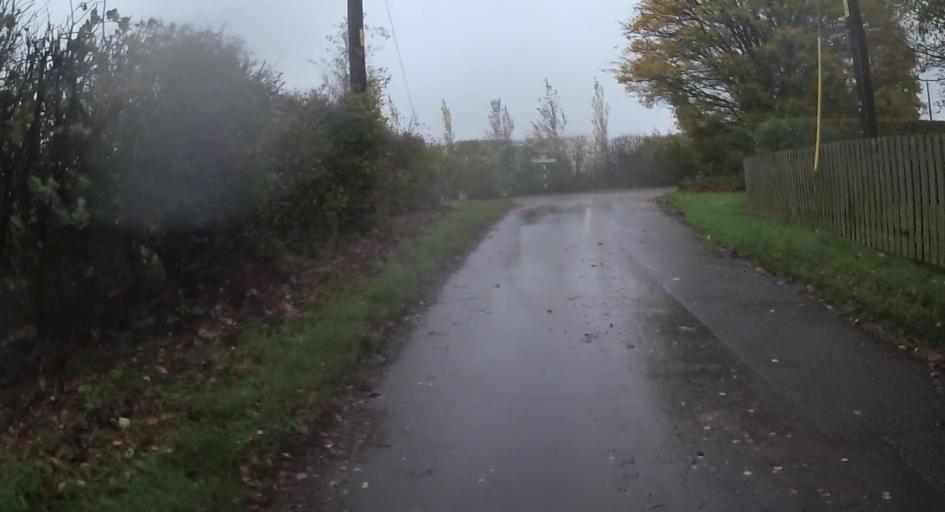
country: GB
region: England
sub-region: Hampshire
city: Four Marks
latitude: 51.1299
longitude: -1.0925
